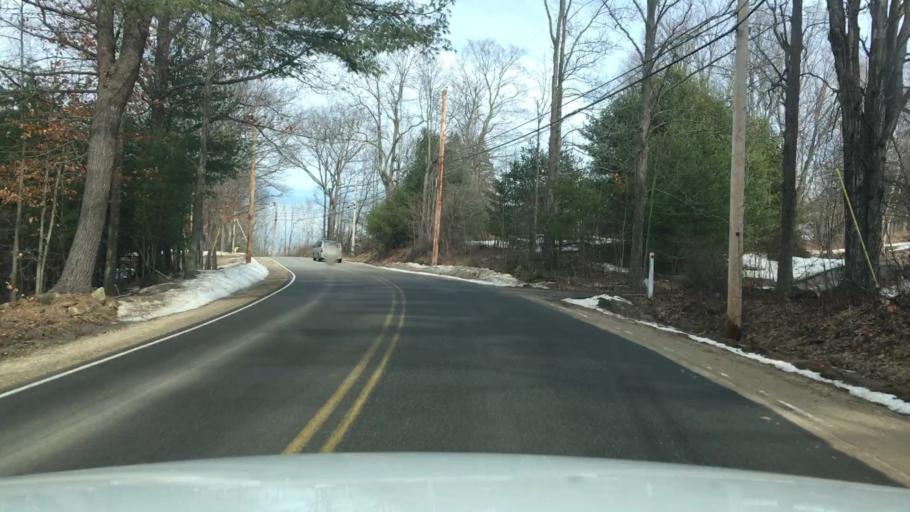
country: US
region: Maine
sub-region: York County
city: Springvale
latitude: 43.4896
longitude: -70.8072
